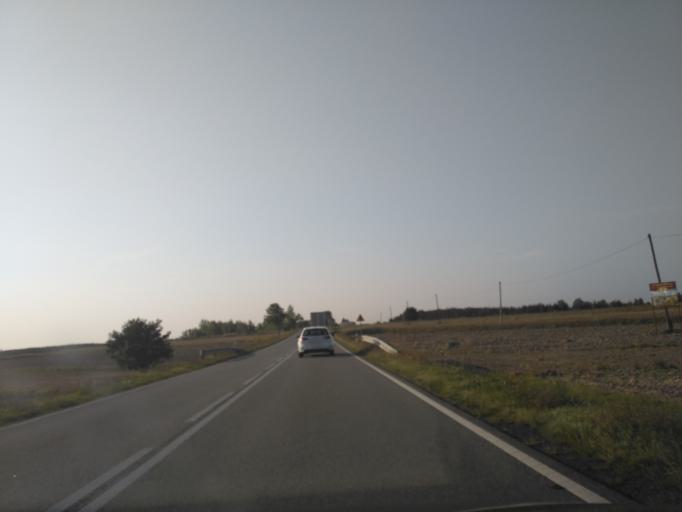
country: PL
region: Lublin Voivodeship
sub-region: Powiat janowski
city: Modliborzyce
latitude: 50.7851
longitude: 22.3215
